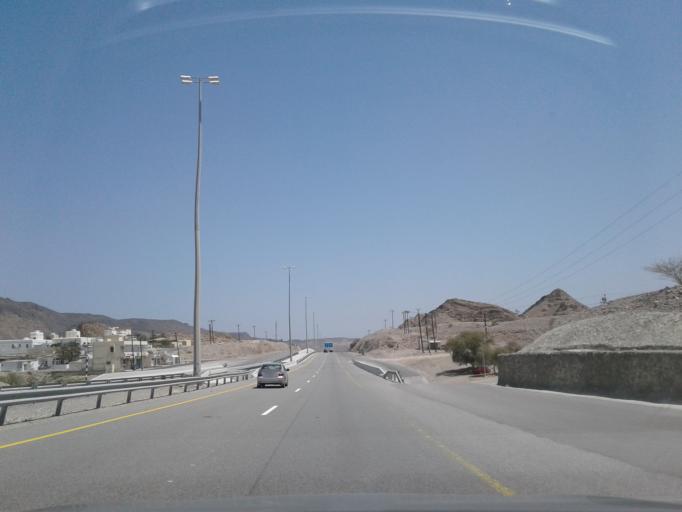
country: OM
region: Muhafazat Masqat
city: Muscat
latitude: 23.2581
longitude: 58.7722
